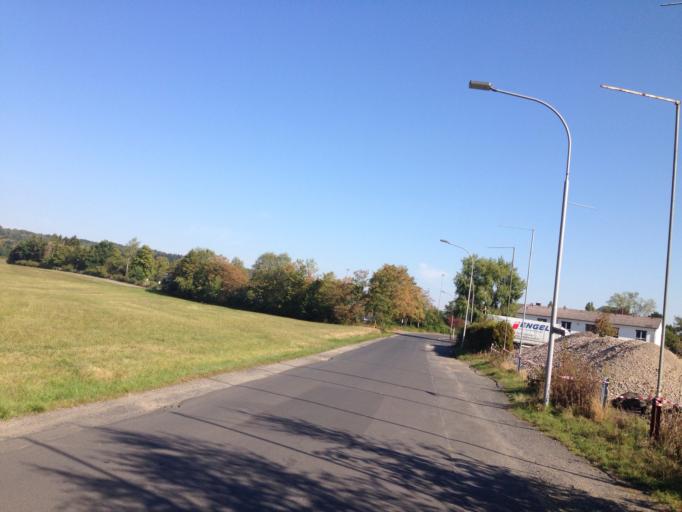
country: DE
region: Hesse
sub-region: Regierungsbezirk Giessen
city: Giessen
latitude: 50.5439
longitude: 8.7067
